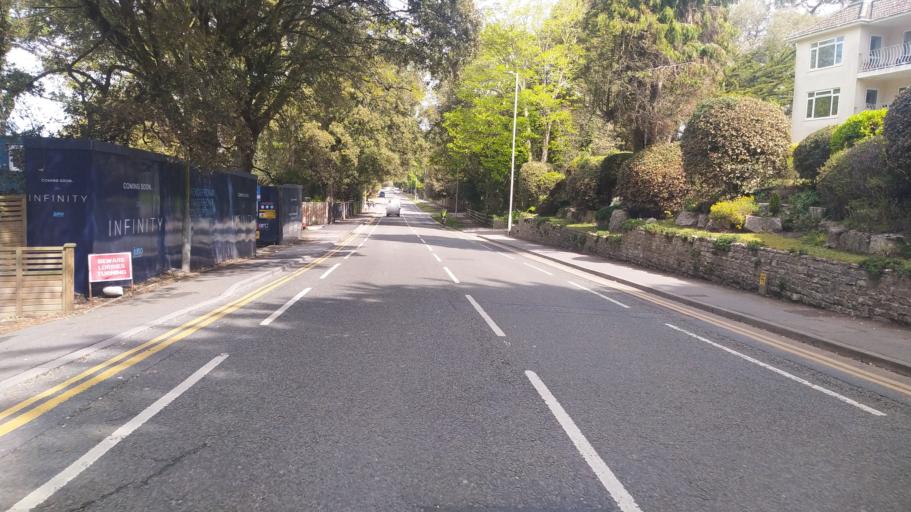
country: GB
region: England
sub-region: Dorset
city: Parkstone
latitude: 50.7043
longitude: -1.9436
